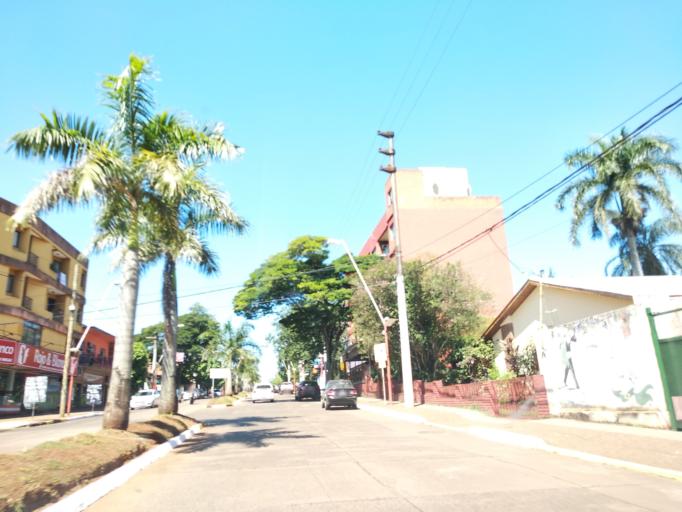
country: AR
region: Misiones
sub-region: Departamento de Iguazu
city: Puerto Iguazu
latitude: -25.6055
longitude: -54.5688
